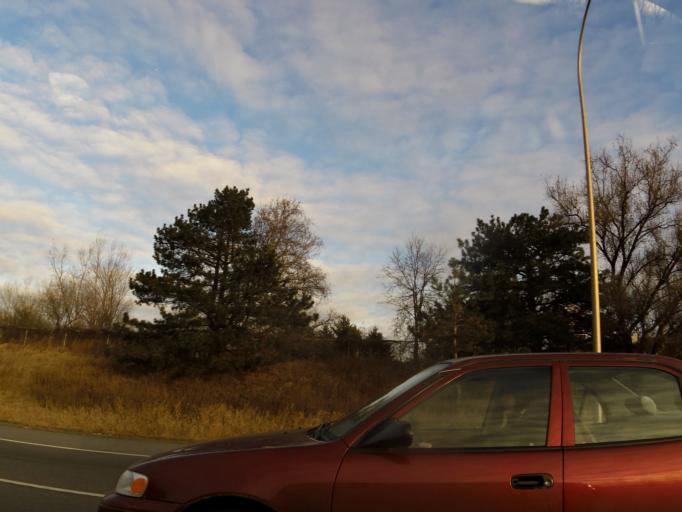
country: US
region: Minnesota
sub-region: Hennepin County
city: Saint Anthony
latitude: 45.0315
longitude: -93.1909
